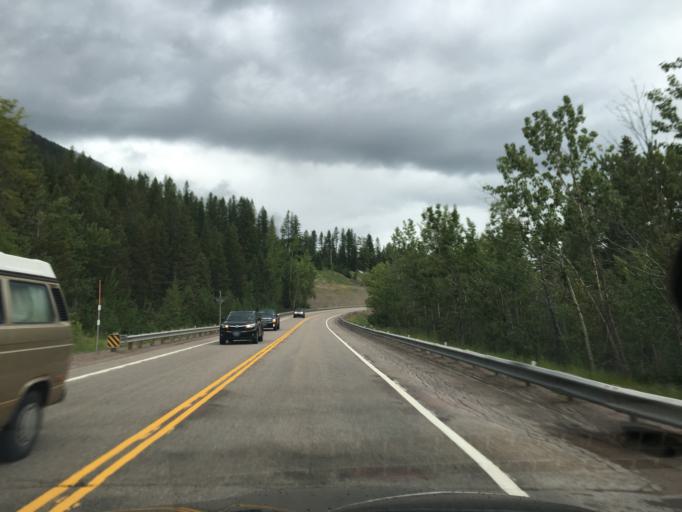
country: US
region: Montana
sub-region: Flathead County
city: Bigfork
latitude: 48.2774
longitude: -113.6061
